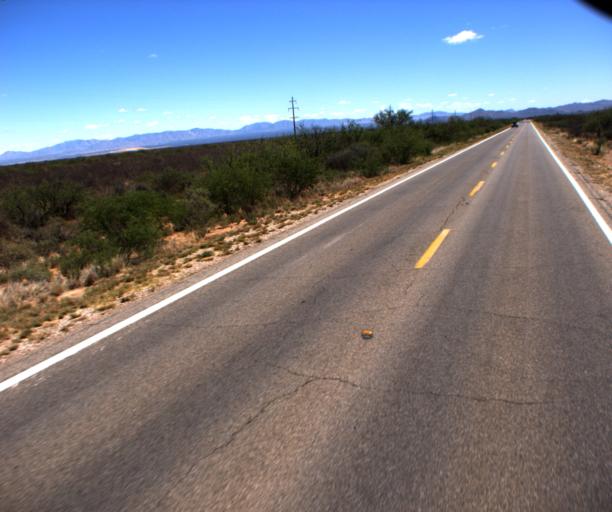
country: US
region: Arizona
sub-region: Cochise County
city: Huachuca City
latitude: 31.6933
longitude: -110.3262
